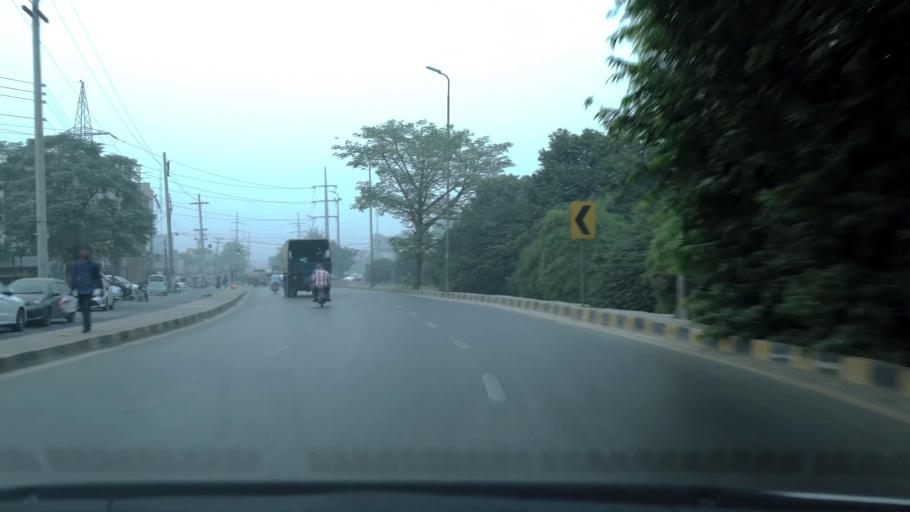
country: PK
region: Punjab
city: Lahore
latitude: 31.4769
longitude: 74.3013
